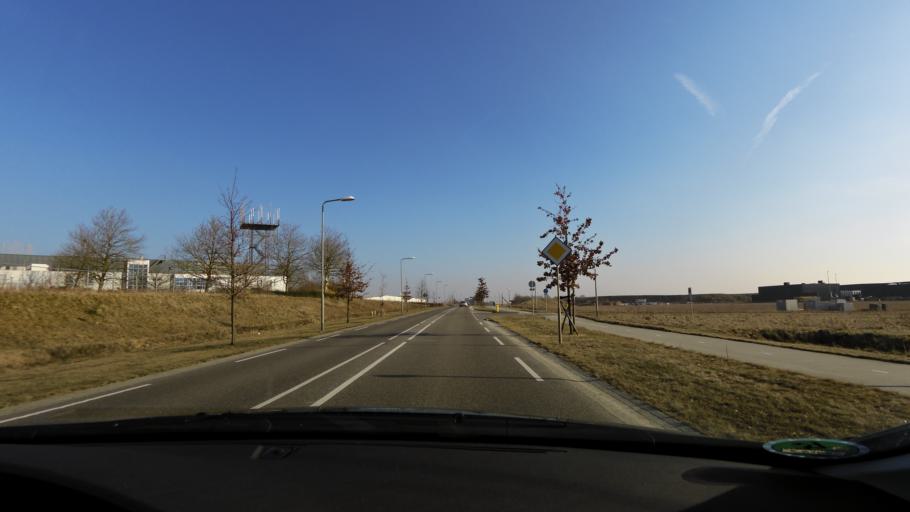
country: NL
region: Limburg
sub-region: Gemeente Beek
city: Beek
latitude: 50.9160
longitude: 5.7848
